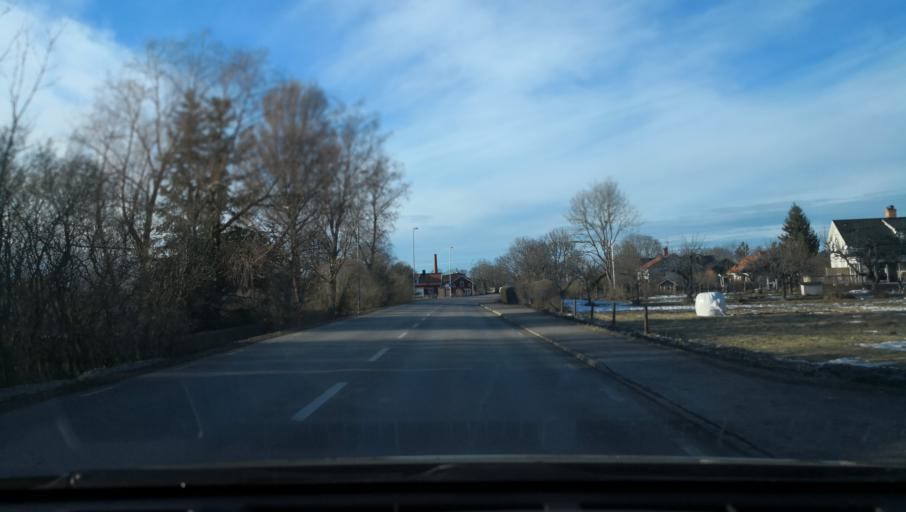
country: SE
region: Uppsala
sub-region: Osthammars Kommun
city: OEsthammar
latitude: 60.2851
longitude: 18.2901
